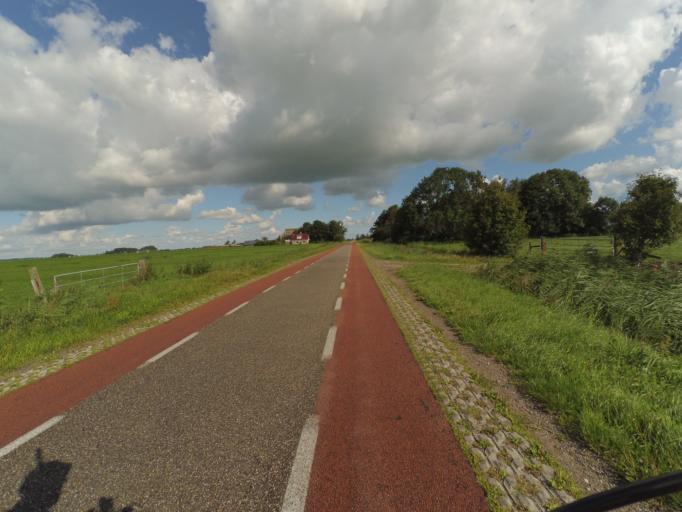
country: NL
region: Friesland
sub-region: Gemeente Dantumadiel
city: Feanwalden
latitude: 53.2561
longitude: 5.9631
